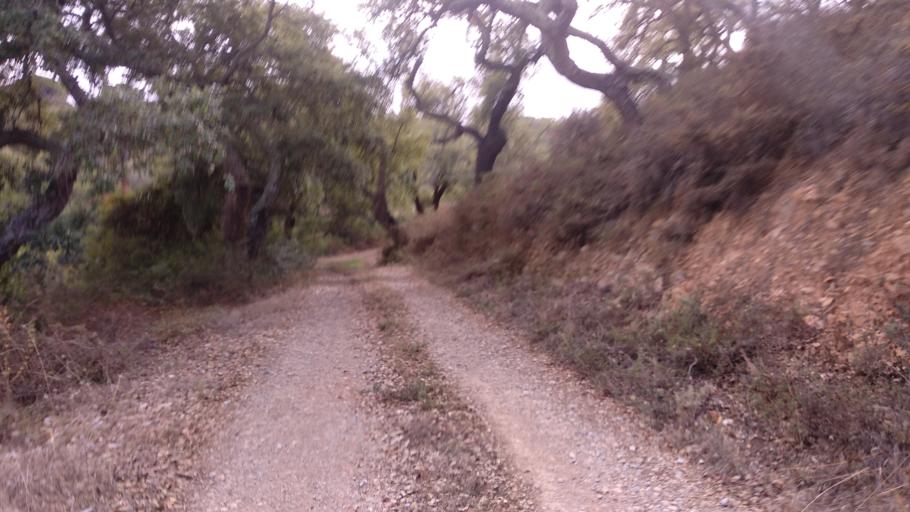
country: PT
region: Faro
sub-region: Sao Bras de Alportel
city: Sao Bras de Alportel
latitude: 37.1625
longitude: -7.9060
